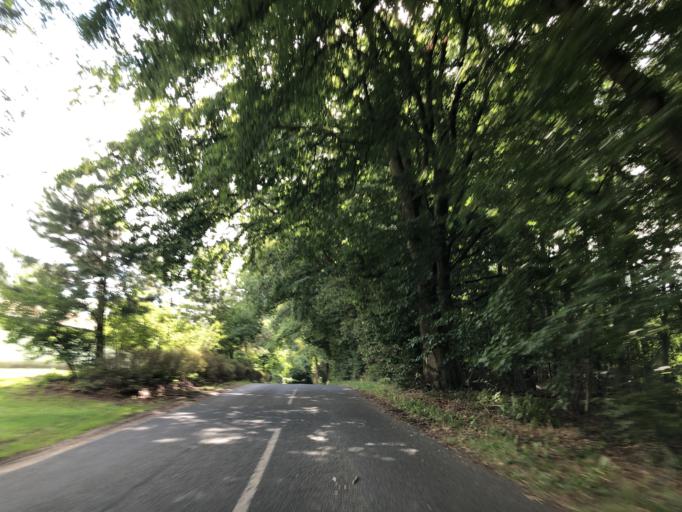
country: DK
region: North Denmark
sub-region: Vesthimmerland Kommune
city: Alestrup
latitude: 56.6063
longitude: 9.4343
